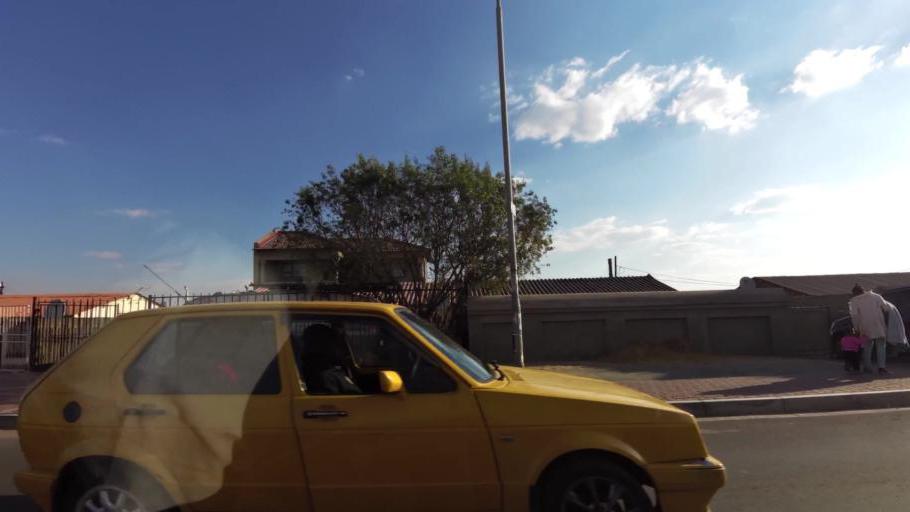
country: ZA
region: Gauteng
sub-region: City of Johannesburg Metropolitan Municipality
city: Soweto
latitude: -26.2272
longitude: 27.8938
